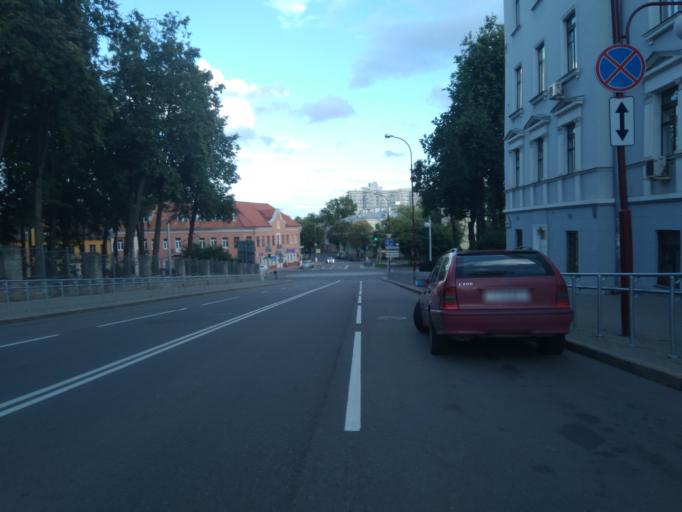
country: BY
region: Minsk
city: Minsk
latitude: 53.8986
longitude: 27.5686
